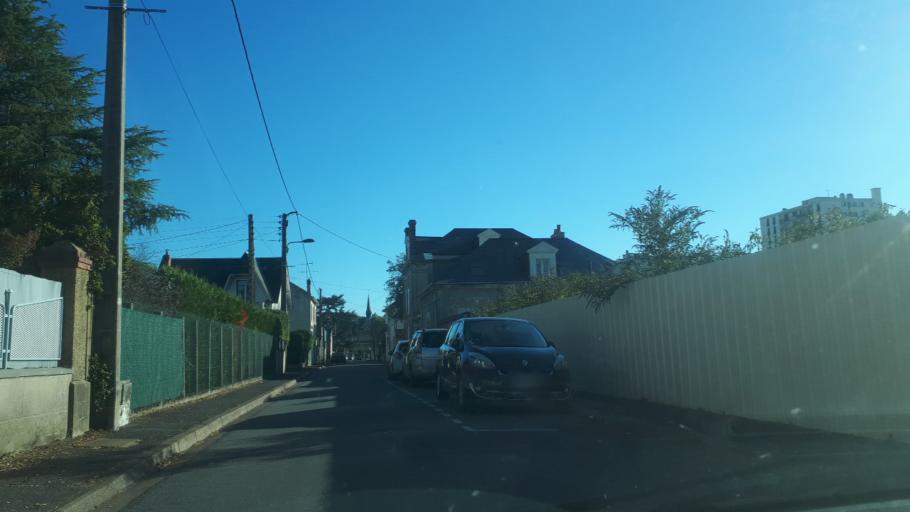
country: FR
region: Centre
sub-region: Departement du Loir-et-Cher
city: Vendome
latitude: 47.8006
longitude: 1.0667
